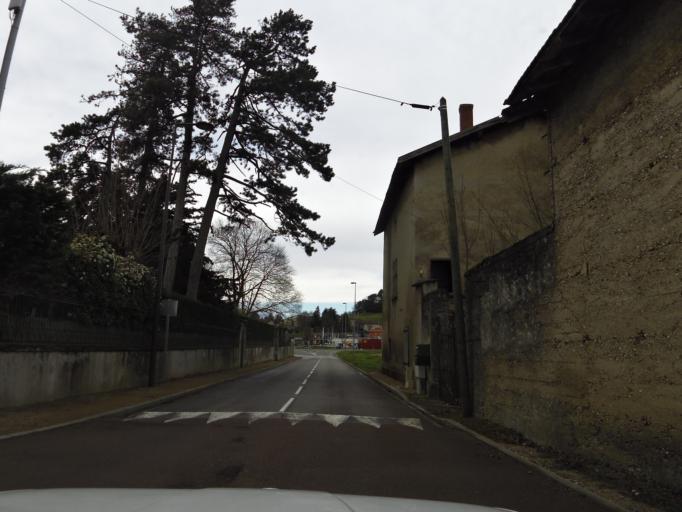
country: FR
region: Rhone-Alpes
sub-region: Departement de l'Ain
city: Meximieux
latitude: 45.9010
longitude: 5.2011
